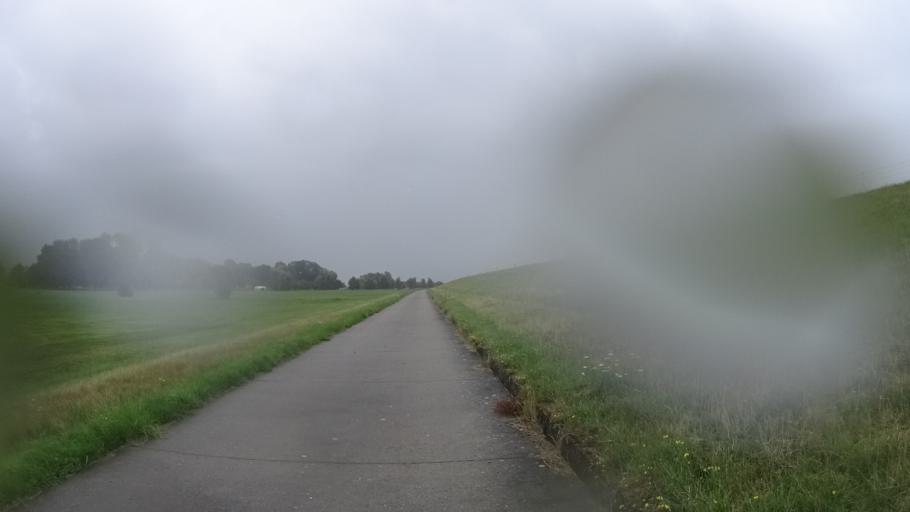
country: DE
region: Lower Saxony
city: Hitzacker
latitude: 53.1835
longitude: 11.0147
